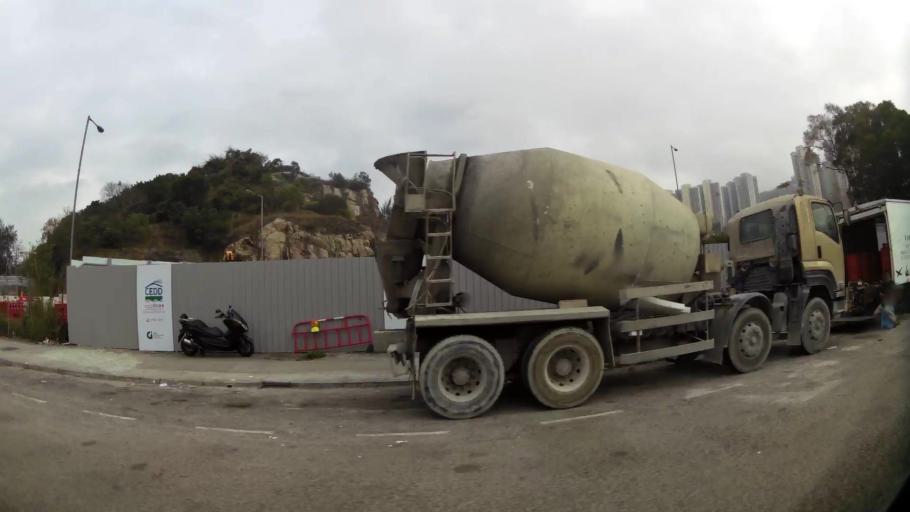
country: HK
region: Kowloon City
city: Kowloon
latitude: 22.2986
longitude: 114.2289
